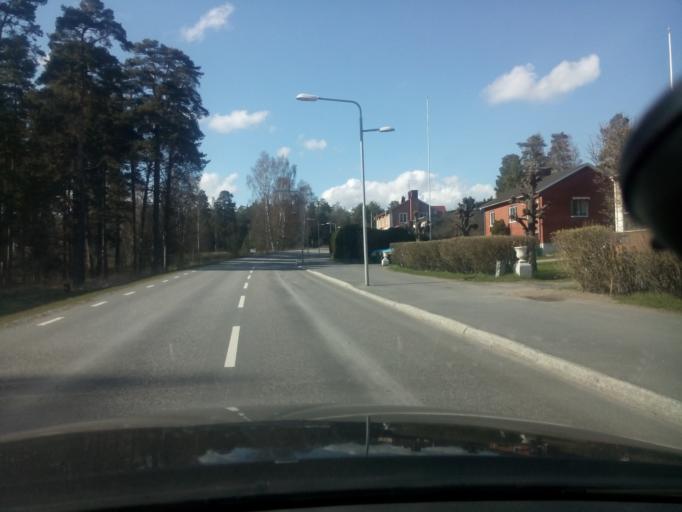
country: SE
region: Soedermanland
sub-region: Flens Kommun
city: Malmkoping
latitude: 59.1392
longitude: 16.7192
